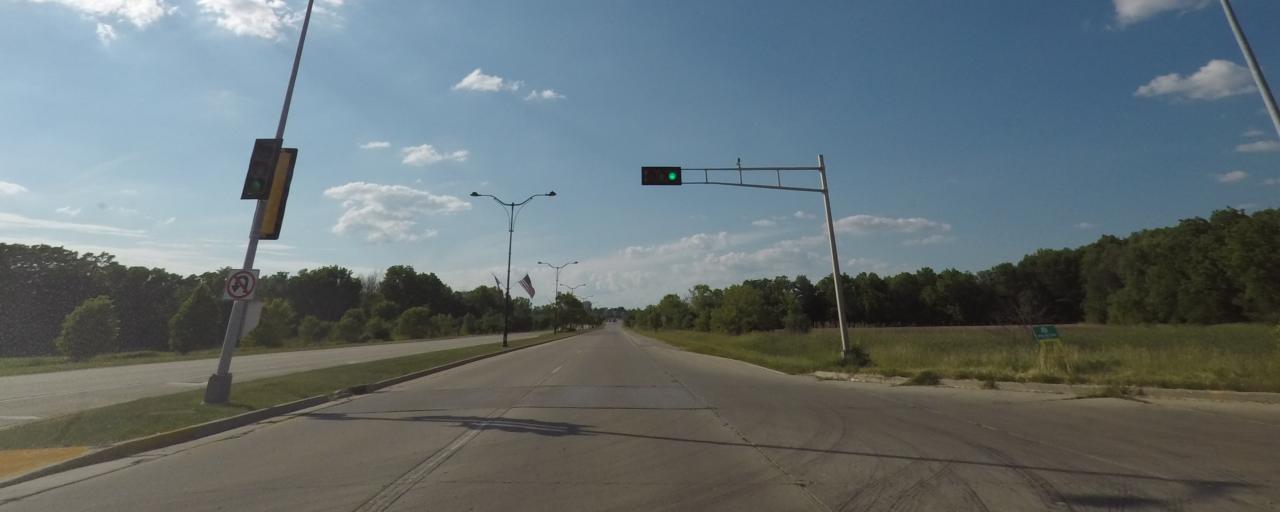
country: US
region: Wisconsin
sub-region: Waukesha County
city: Muskego
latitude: 42.9211
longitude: -88.1099
